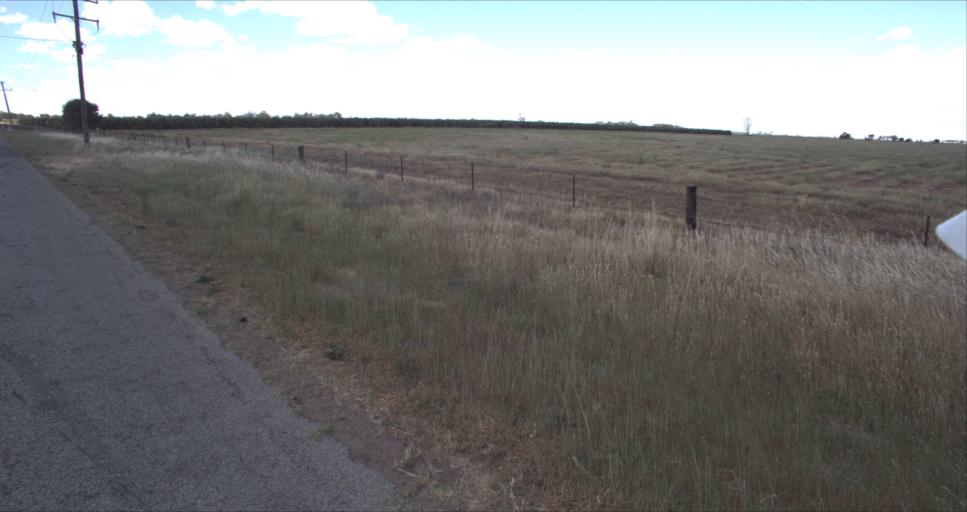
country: AU
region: New South Wales
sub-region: Leeton
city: Leeton
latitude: -34.5258
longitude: 146.2212
